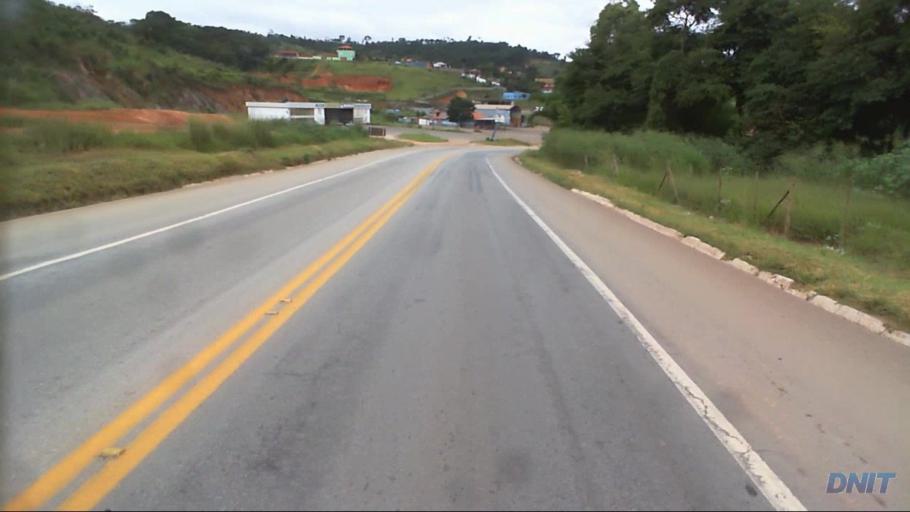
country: BR
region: Minas Gerais
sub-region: Joao Monlevade
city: Joao Monlevade
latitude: -19.8449
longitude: -43.2034
